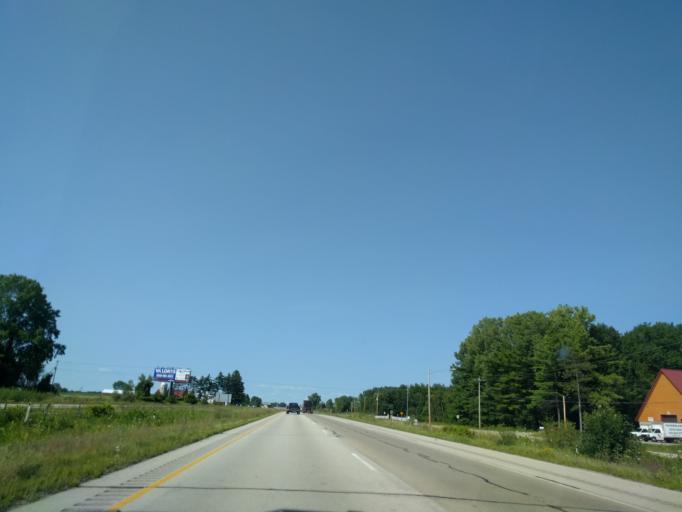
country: US
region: Wisconsin
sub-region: Brown County
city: Suamico
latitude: 44.6511
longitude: -88.0499
